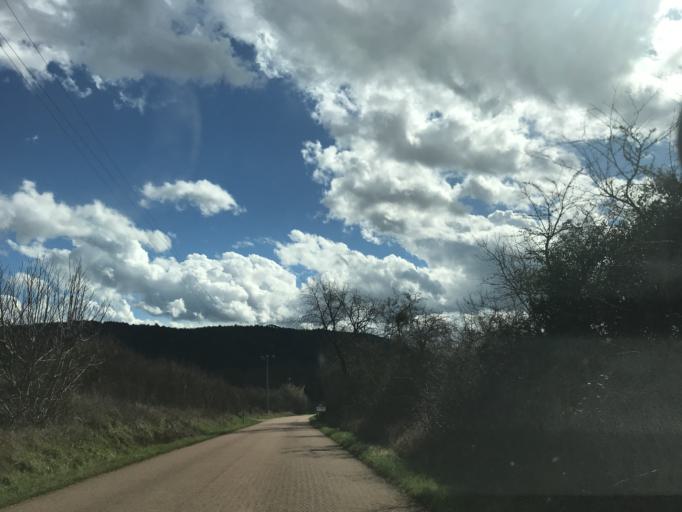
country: FR
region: Bourgogne
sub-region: Departement de la Nievre
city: Clamecy
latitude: 47.4829
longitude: 3.5201
